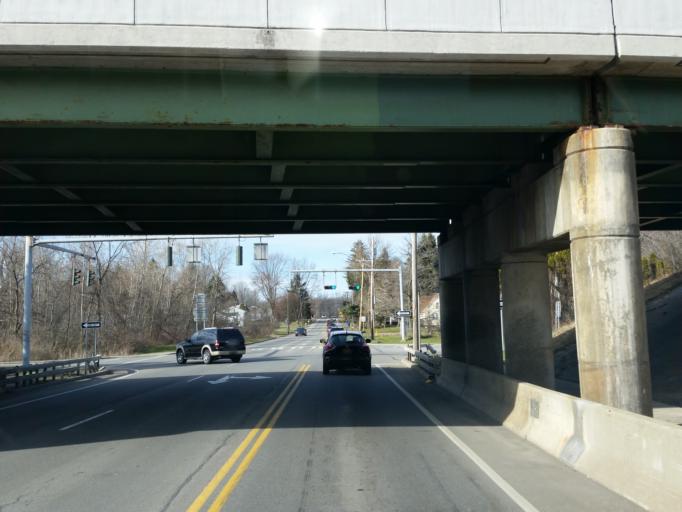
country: US
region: New York
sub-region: Monroe County
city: North Gates
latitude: 43.1211
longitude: -77.7456
